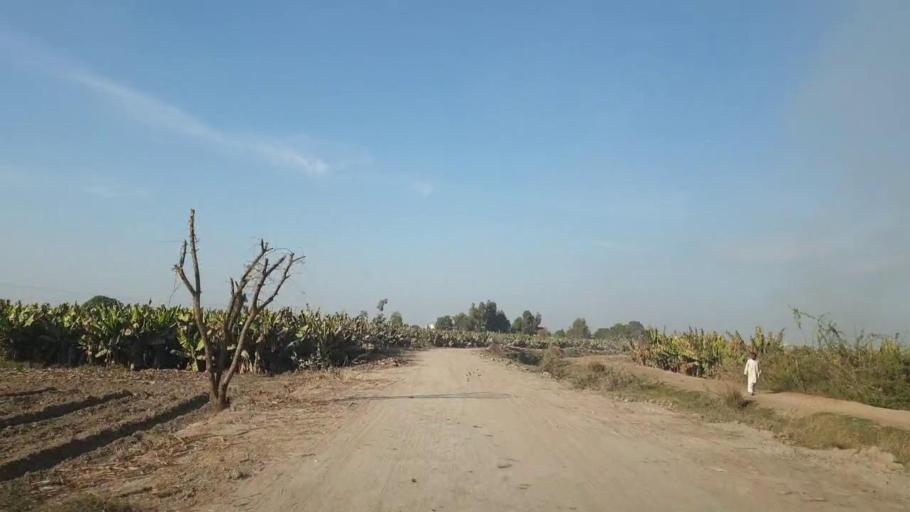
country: PK
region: Sindh
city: Tando Adam
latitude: 25.7059
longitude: 68.7021
